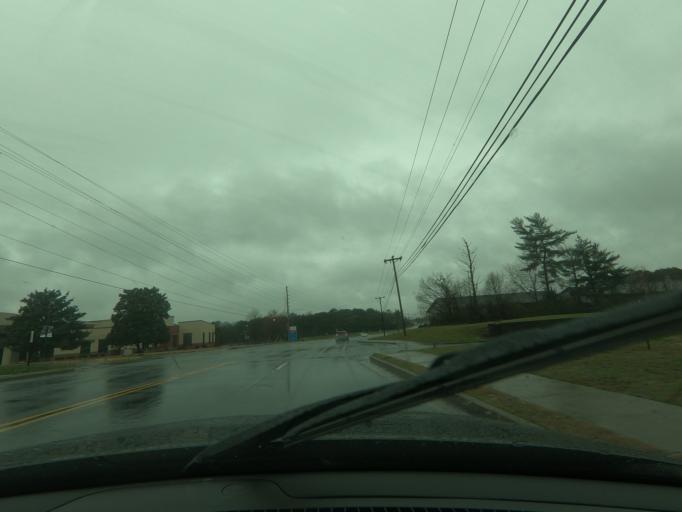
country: US
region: Georgia
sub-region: Gordon County
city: Calhoun
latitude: 34.5120
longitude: -84.9254
